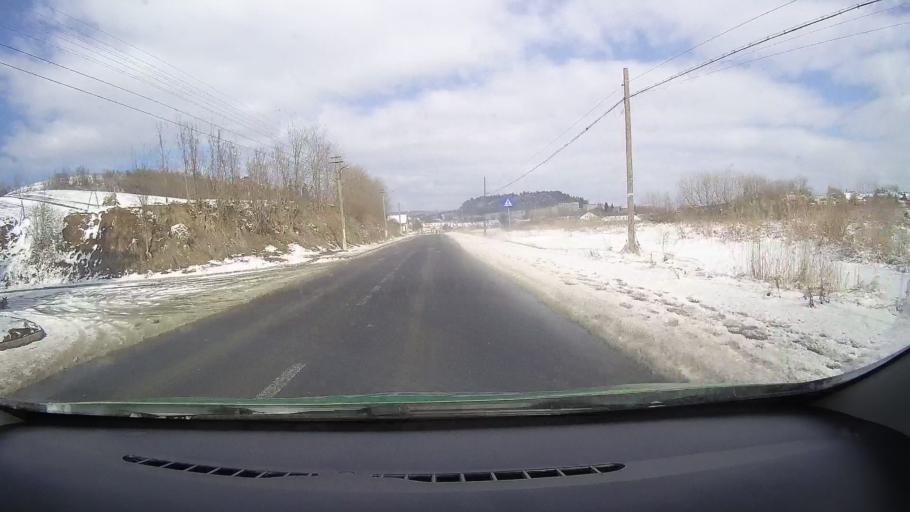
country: RO
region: Sibiu
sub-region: Oras Agnita
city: Agnita
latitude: 45.9722
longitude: 24.6078
